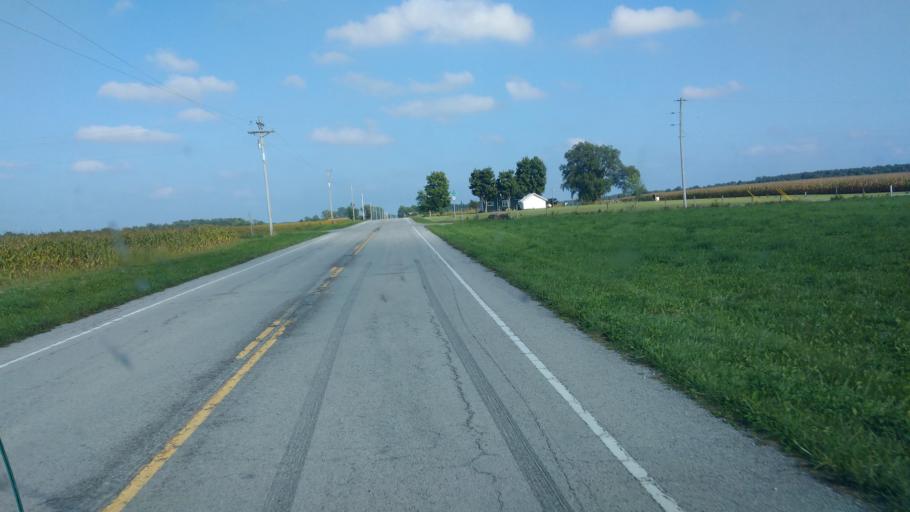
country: US
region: Ohio
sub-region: Hancock County
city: Arlington
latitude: 40.8336
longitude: -83.6009
